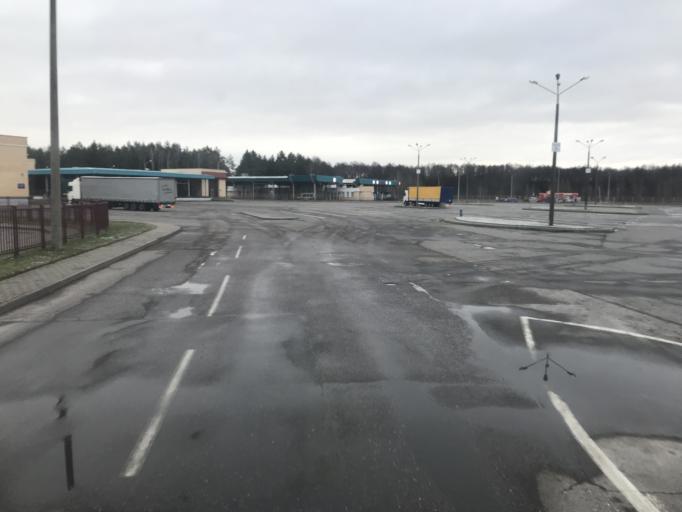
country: BY
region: Grodnenskaya
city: Vyalikaya Byerastavitsa
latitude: 53.1225
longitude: 23.8966
